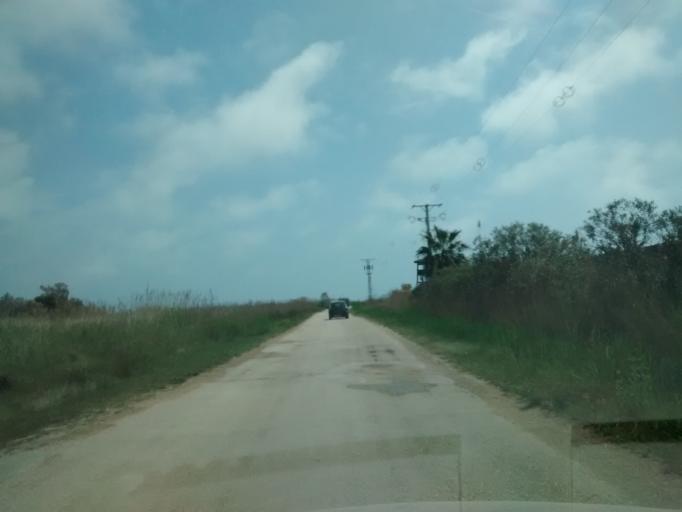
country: ES
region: Catalonia
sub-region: Provincia de Tarragona
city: Deltebre
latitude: 40.6881
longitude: 0.8483
